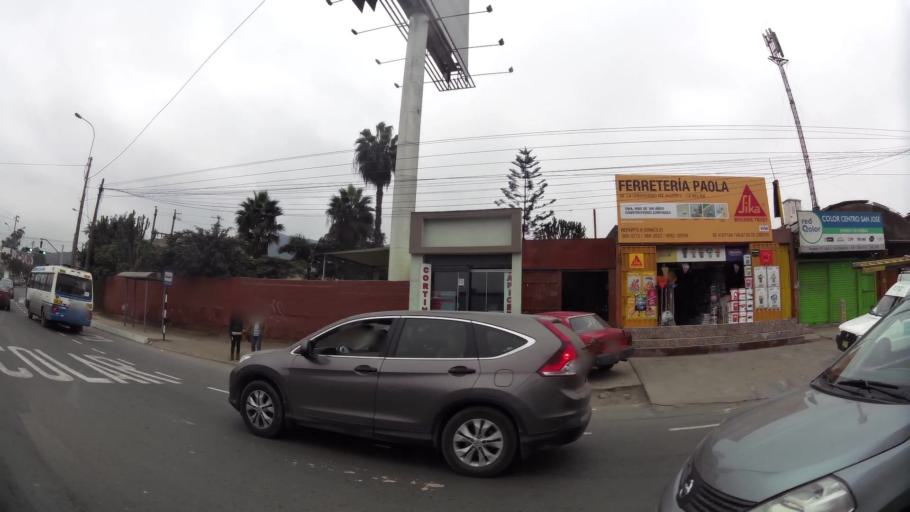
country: PE
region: Lima
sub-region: Lima
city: La Molina
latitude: -12.0845
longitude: -76.9271
